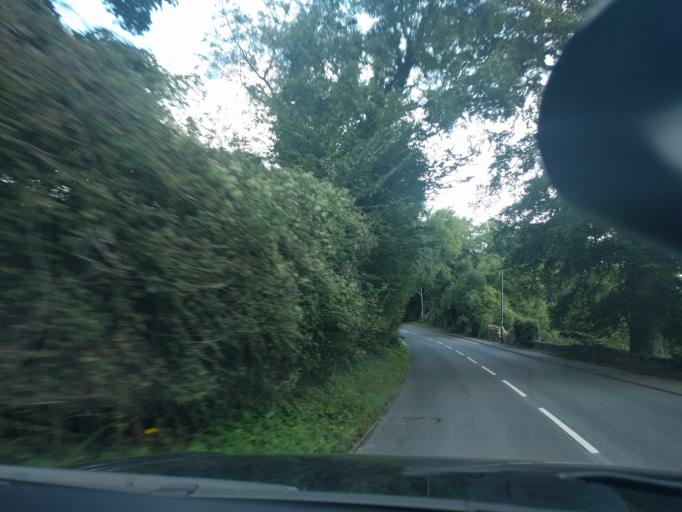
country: GB
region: England
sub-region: Bath and North East Somerset
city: Freshford
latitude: 51.3706
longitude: -2.3181
